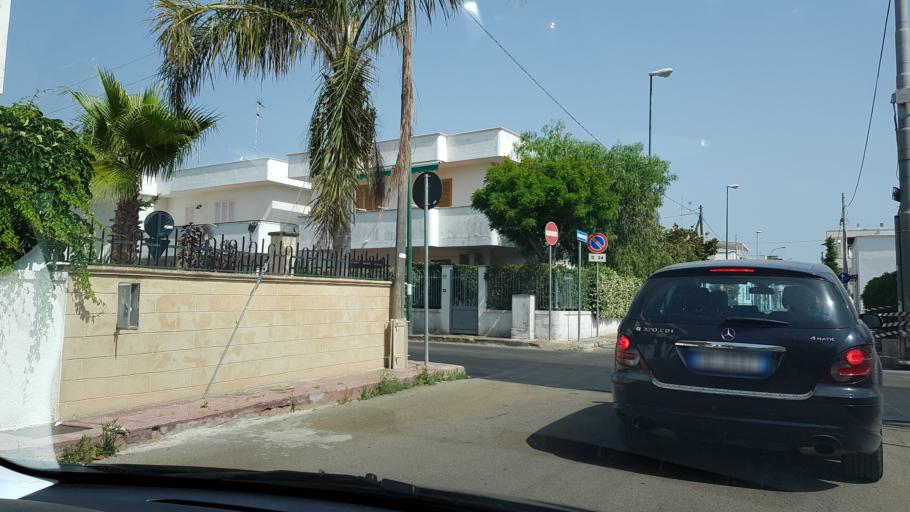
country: IT
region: Apulia
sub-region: Provincia di Lecce
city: Porto Cesareo
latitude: 40.2653
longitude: 17.8898
